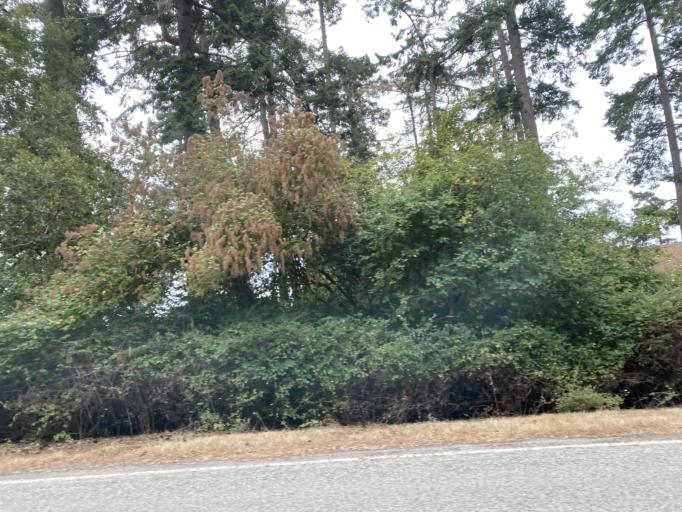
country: US
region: Washington
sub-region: Island County
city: Coupeville
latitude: 48.2391
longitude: -122.6902
